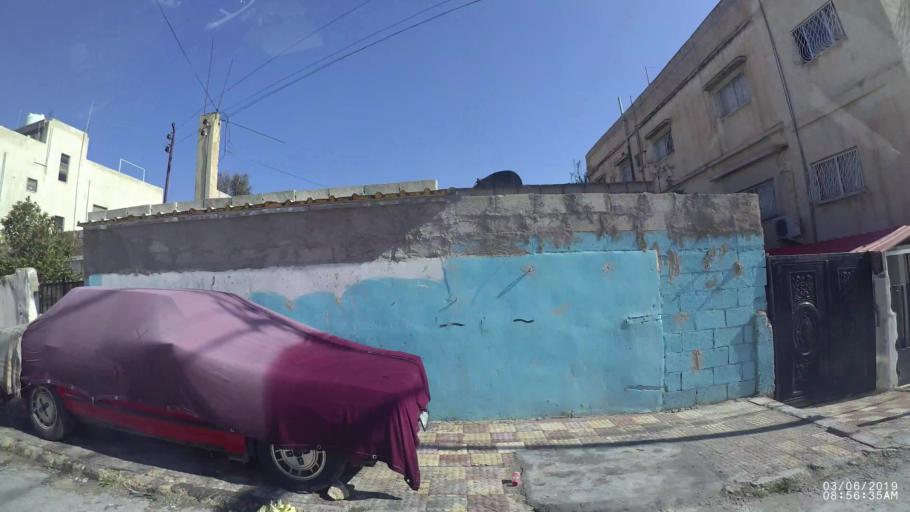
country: JO
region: Amman
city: Amman
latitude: 31.9904
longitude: 35.9919
